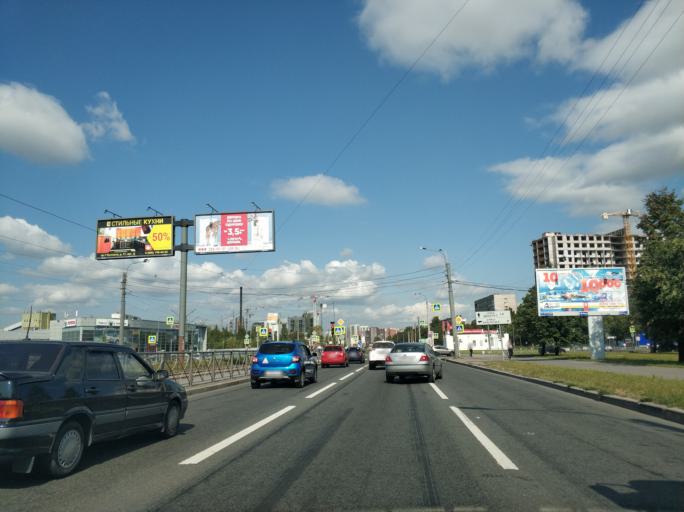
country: RU
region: St.-Petersburg
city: Obukhovo
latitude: 59.8933
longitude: 30.4626
